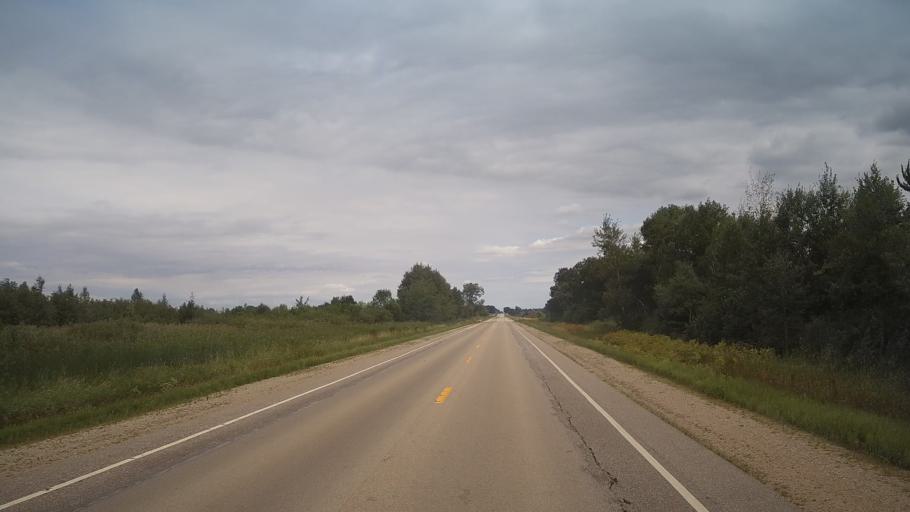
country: US
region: Wisconsin
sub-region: Green Lake County
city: Berlin
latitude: 44.0487
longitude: -88.9653
